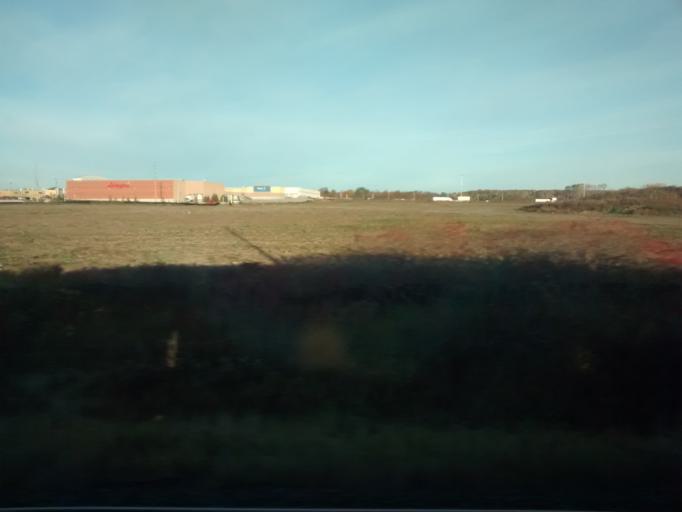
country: CA
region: Ontario
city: Oakville
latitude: 43.3969
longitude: -79.7429
